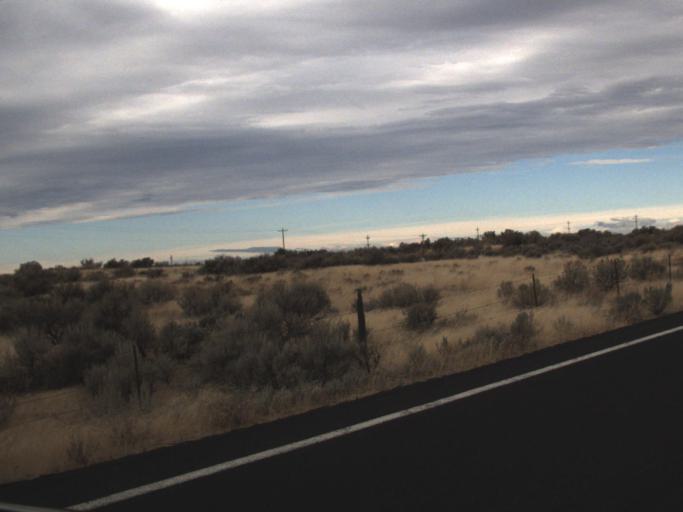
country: US
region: Washington
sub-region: Adams County
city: Ritzville
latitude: 47.4254
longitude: -118.7051
